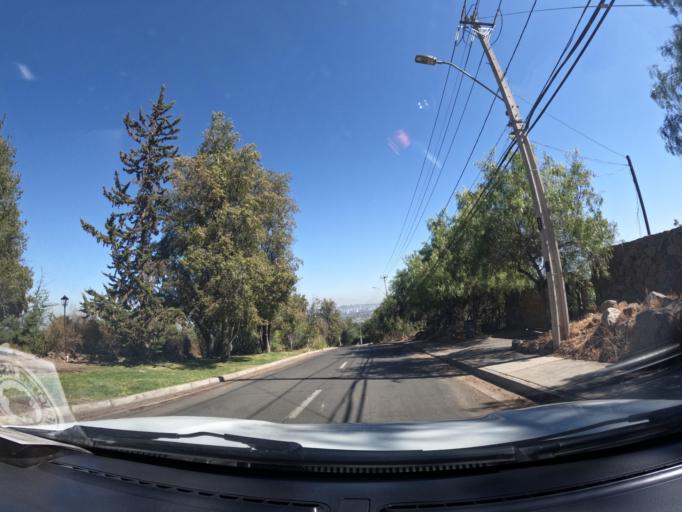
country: CL
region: Santiago Metropolitan
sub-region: Provincia de Santiago
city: Villa Presidente Frei, Nunoa, Santiago, Chile
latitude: -33.4748
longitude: -70.5209
